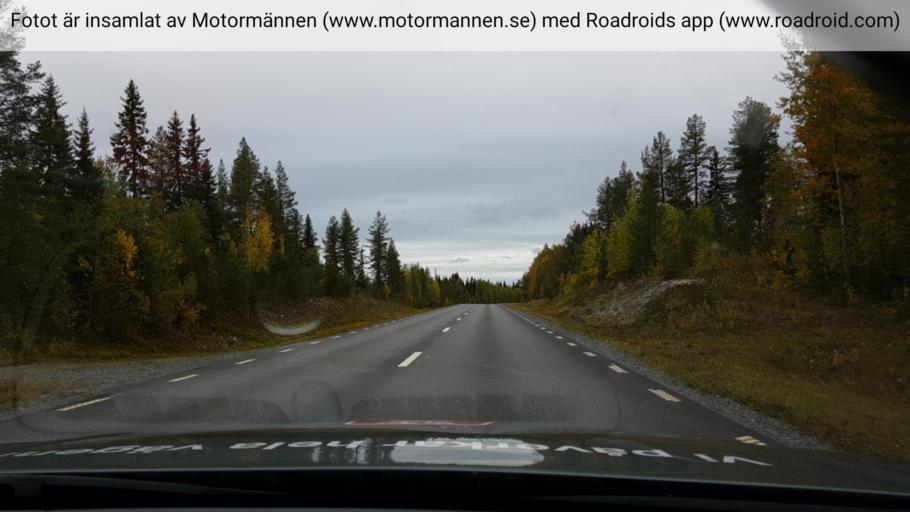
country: SE
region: Vaesterbotten
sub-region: Dorotea Kommun
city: Dorotea
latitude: 64.3143
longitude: 16.6074
